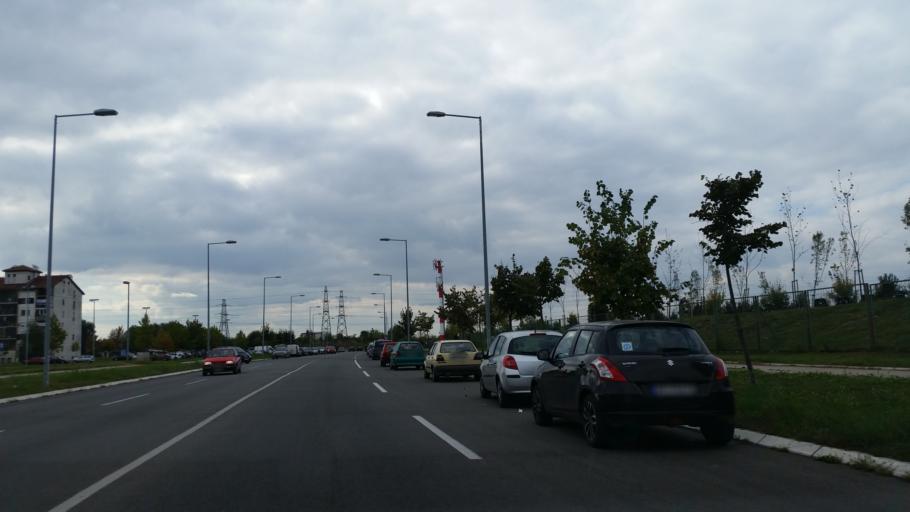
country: RS
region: Central Serbia
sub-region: Belgrade
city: Zemun
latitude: 44.8111
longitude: 20.3640
